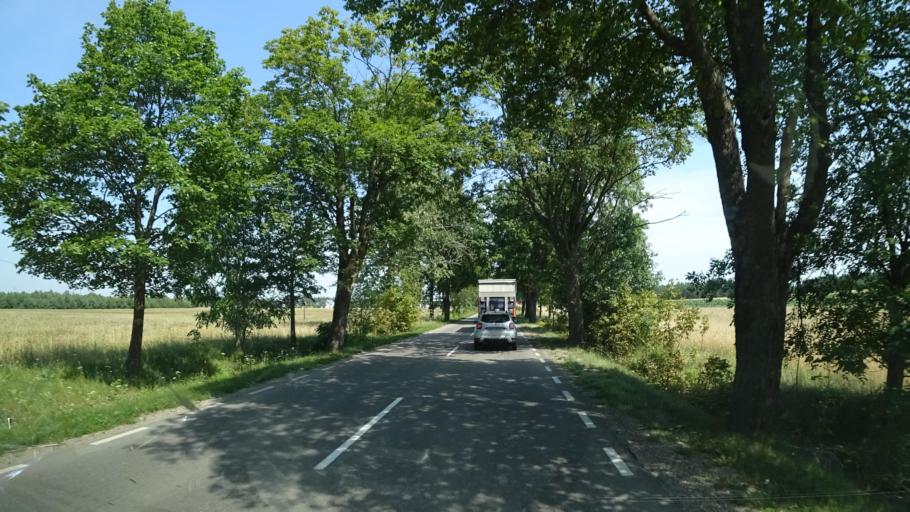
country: PL
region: Pomeranian Voivodeship
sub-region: Powiat koscierski
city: Lipusz
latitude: 54.1277
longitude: 17.8588
